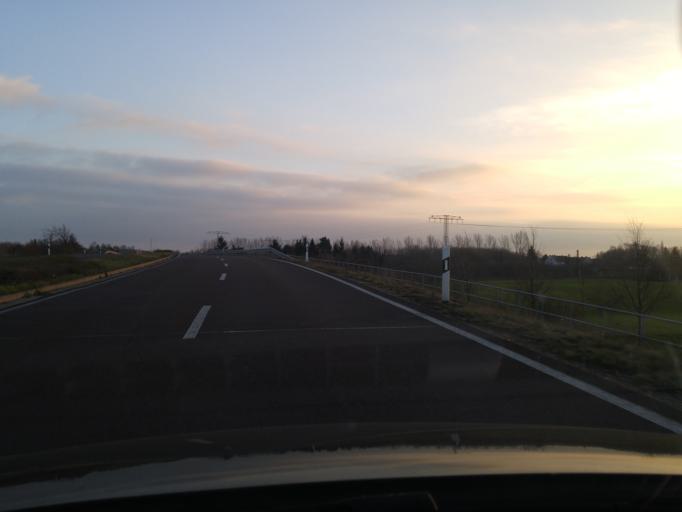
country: DE
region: Saxony
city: Leipzig
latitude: 51.3840
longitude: 12.3410
